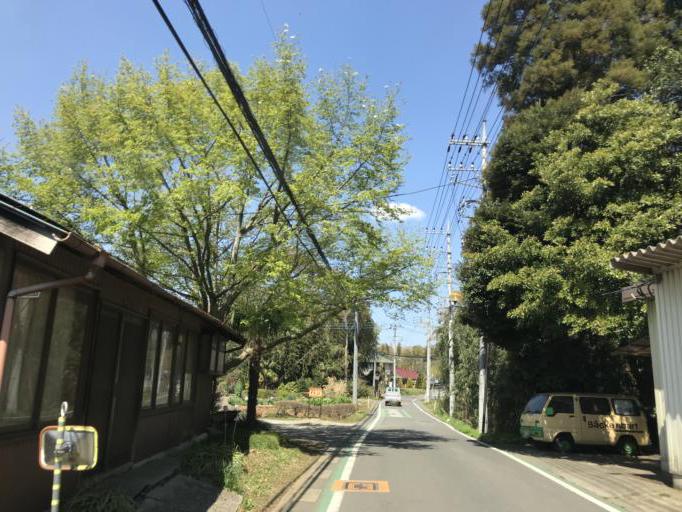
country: JP
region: Ibaraki
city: Moriya
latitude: 35.9281
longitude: 139.9992
